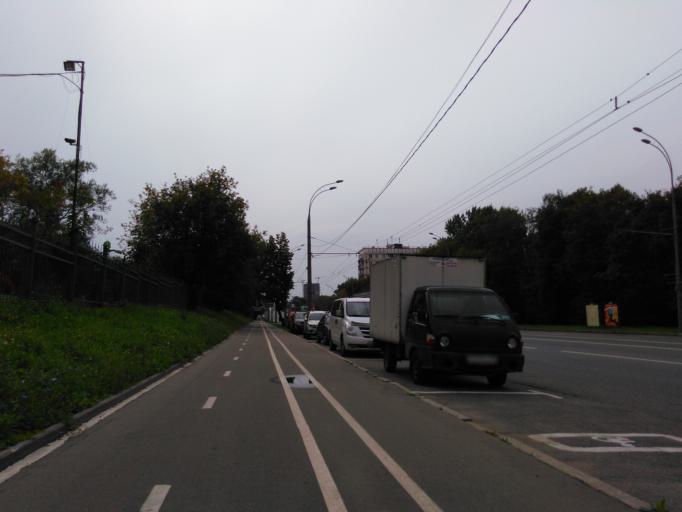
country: RU
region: Moscow
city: Vorob'yovo
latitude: 55.7209
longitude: 37.5253
